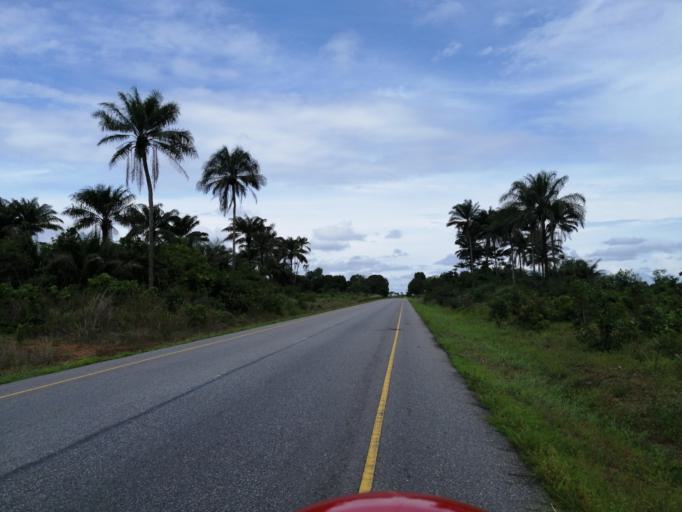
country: SL
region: Northern Province
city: Port Loko
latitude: 8.7381
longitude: -12.9446
